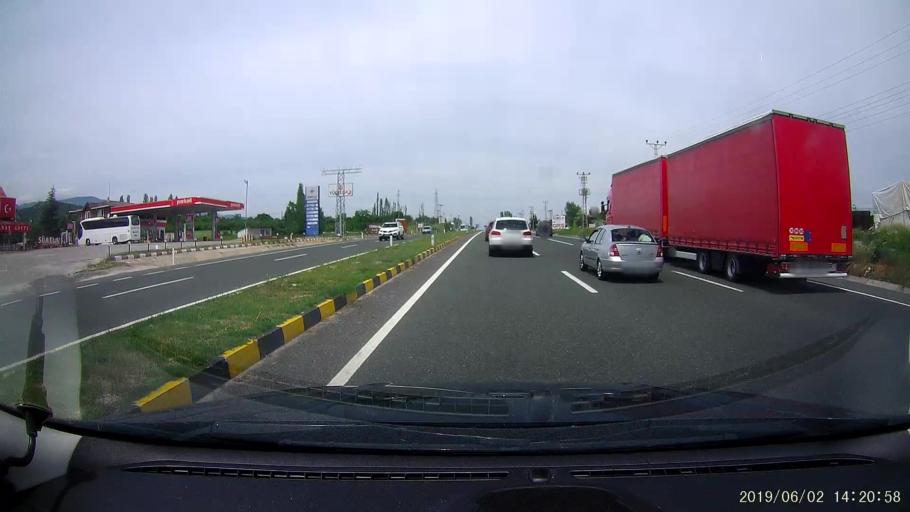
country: TR
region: Kastamonu
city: Tosya
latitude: 40.9744
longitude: 33.9982
